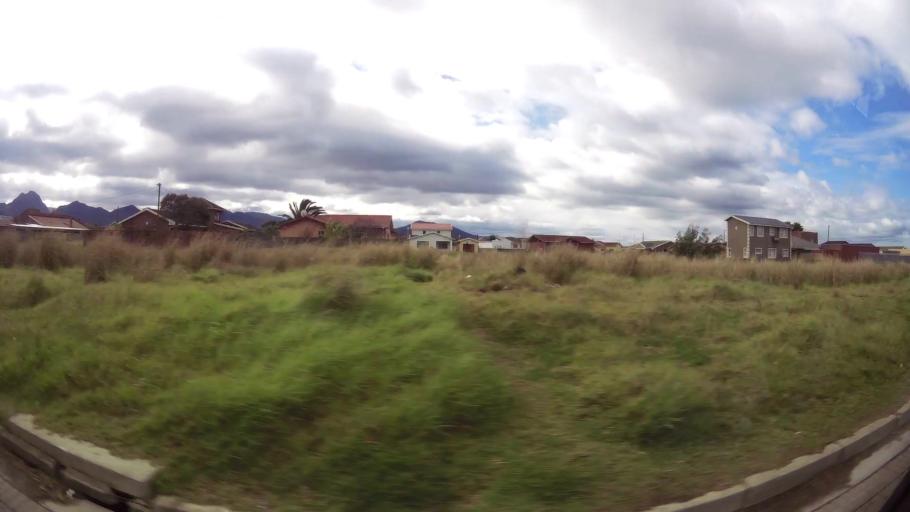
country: ZA
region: Western Cape
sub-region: Eden District Municipality
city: George
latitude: -33.9775
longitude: 22.4907
